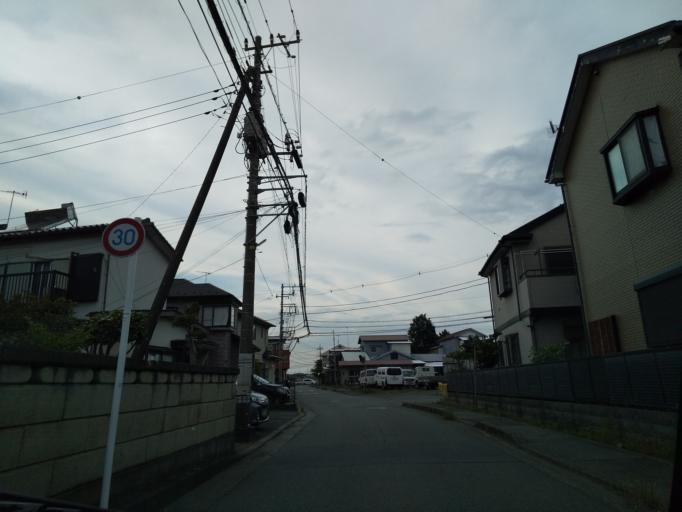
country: JP
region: Kanagawa
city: Atsugi
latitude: 35.4678
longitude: 139.3613
